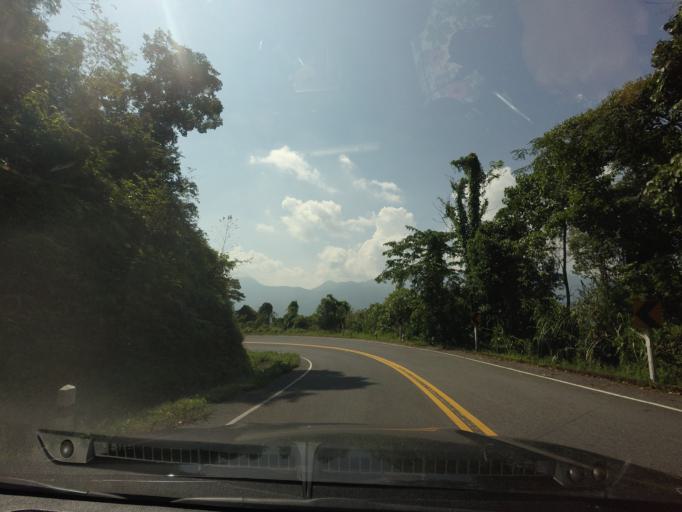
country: TH
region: Nan
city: Bo Kluea
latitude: 19.0393
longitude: 101.0859
